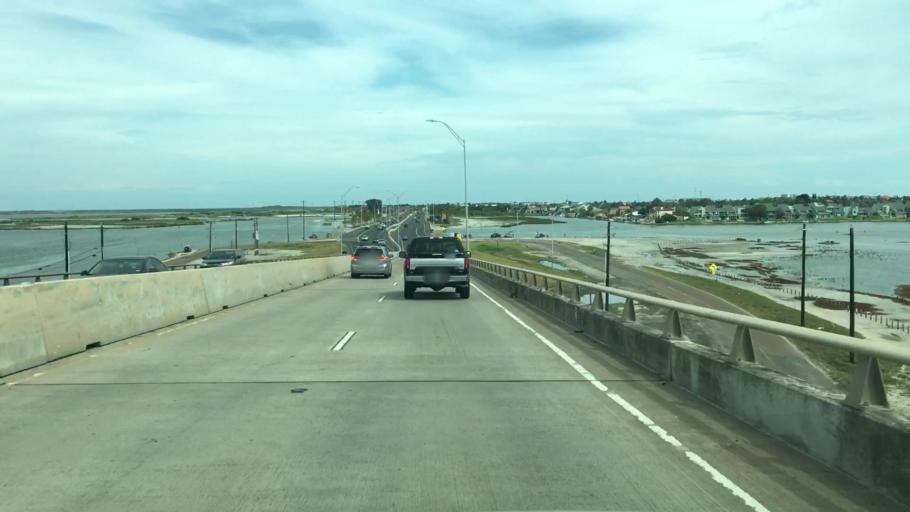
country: US
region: Texas
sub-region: Nueces County
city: Corpus Christi
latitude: 27.6334
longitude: -97.2367
